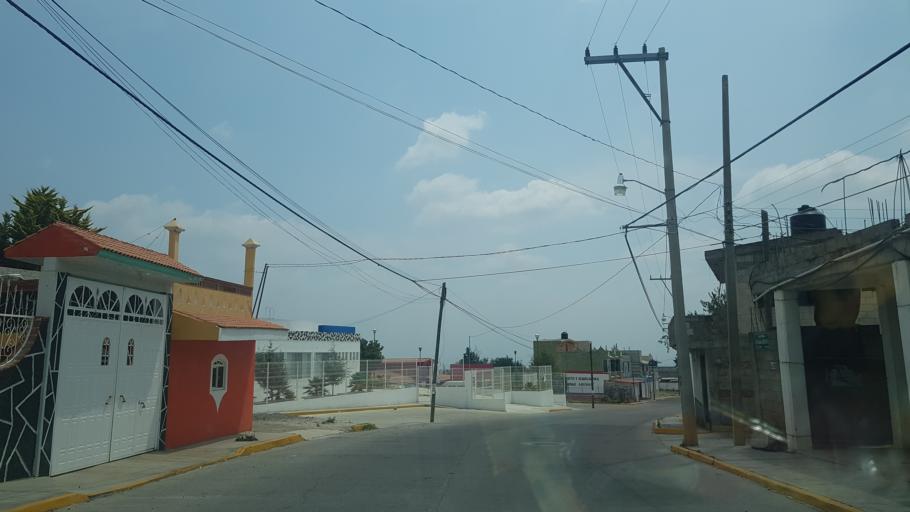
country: MX
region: Puebla
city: Domingo Arenas
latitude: 19.1394
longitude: -98.4496
